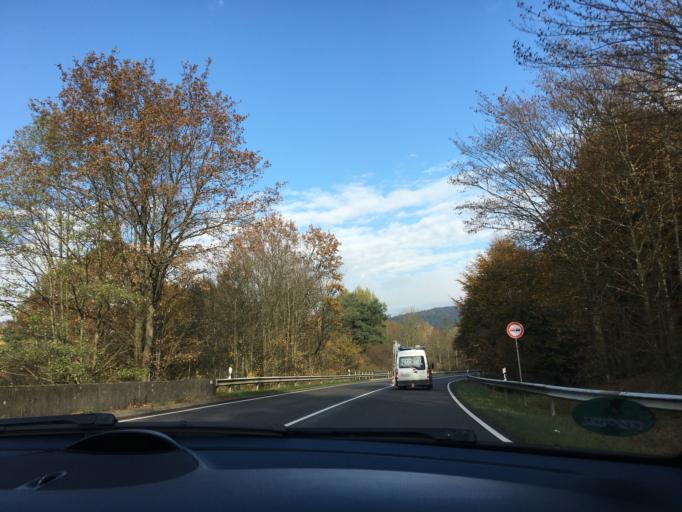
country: DE
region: Rheinland-Pfalz
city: Steinalben
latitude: 49.3169
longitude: 7.6534
